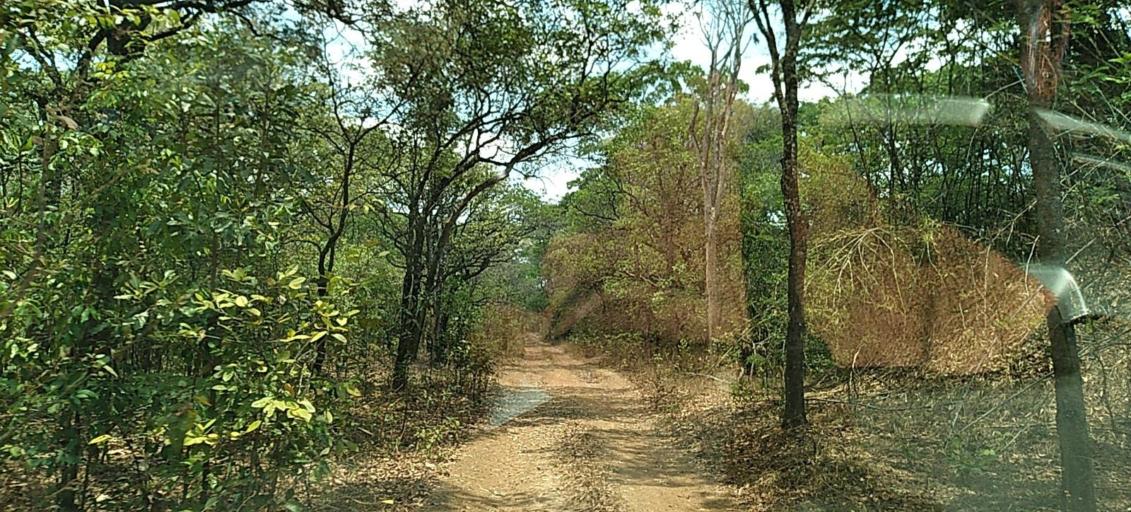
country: ZM
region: Copperbelt
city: Chililabombwe
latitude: -12.4727
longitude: 27.7003
